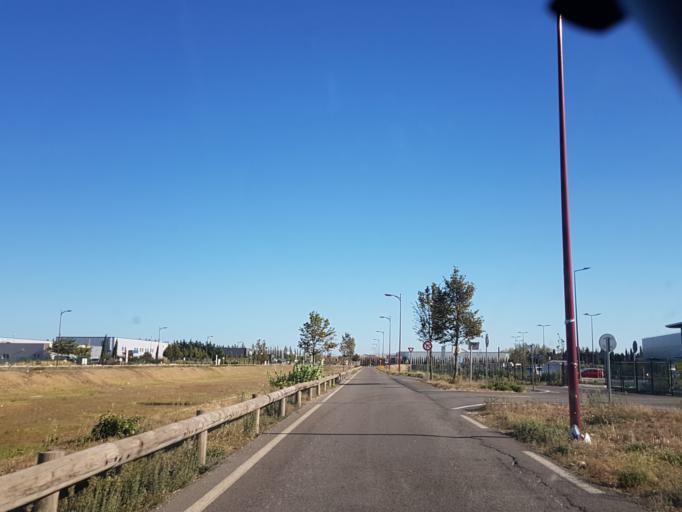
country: FR
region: Provence-Alpes-Cote d'Azur
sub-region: Departement du Vaucluse
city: Entraigues-sur-la-Sorgue
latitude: 43.9885
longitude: 4.9267
